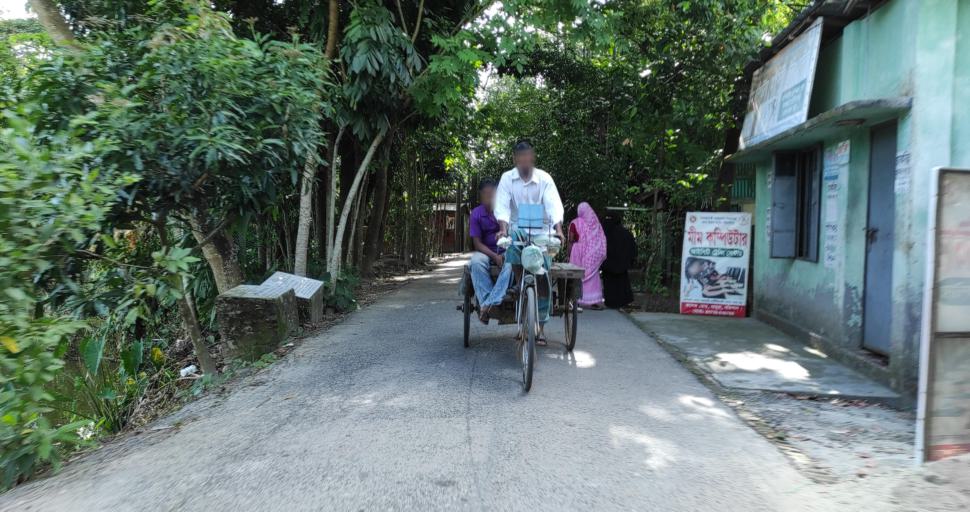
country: BD
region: Barisal
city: Gaurnadi
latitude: 22.8929
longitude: 90.1914
